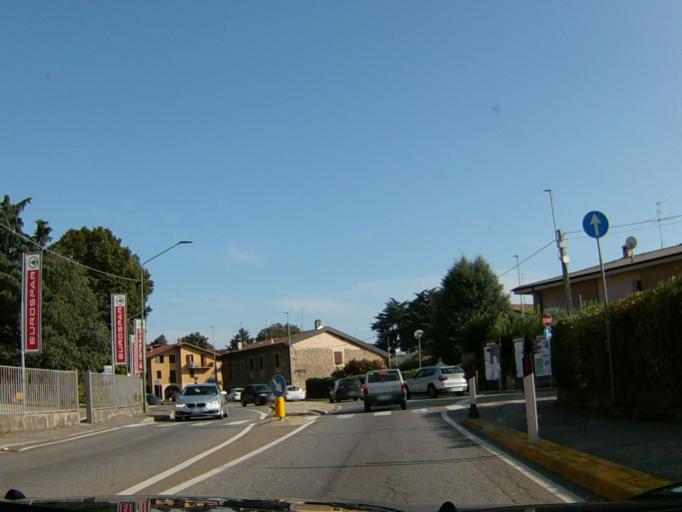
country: IT
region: Lombardy
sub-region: Provincia di Brescia
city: Coccaglio
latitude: 45.5644
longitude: 9.9731
